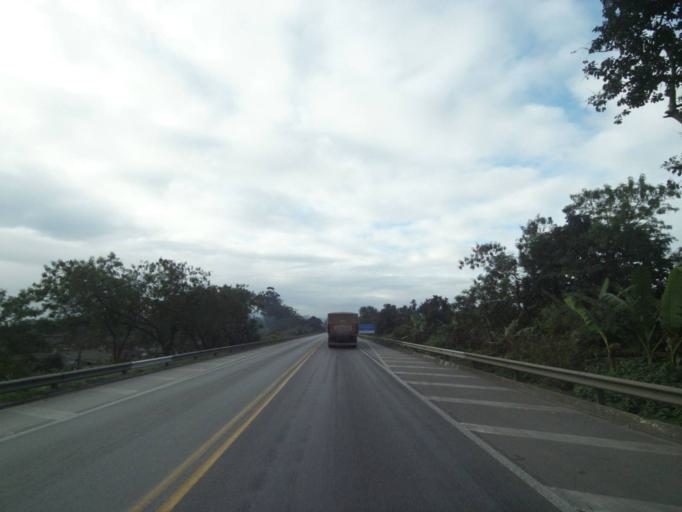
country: BR
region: Parana
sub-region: Paranagua
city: Paranagua
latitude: -25.5501
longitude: -48.5612
